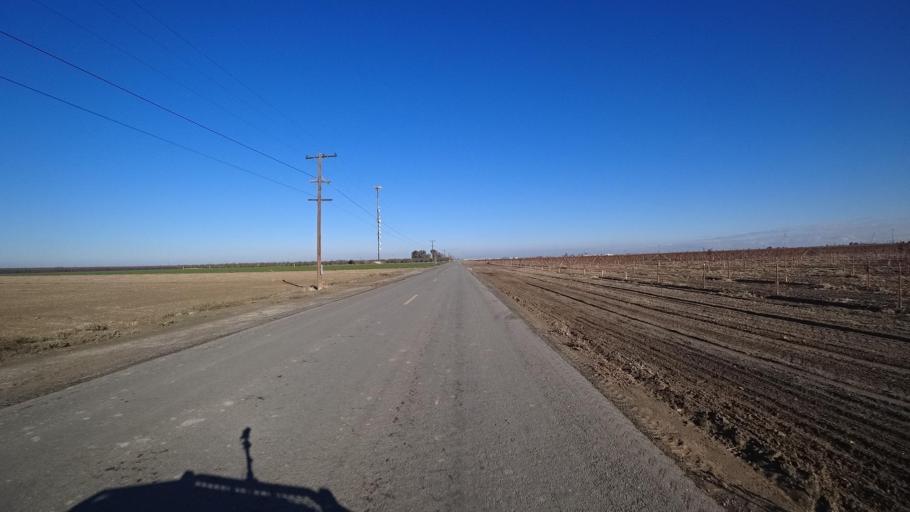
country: US
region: California
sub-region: Kern County
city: Delano
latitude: 35.7496
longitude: -119.3119
